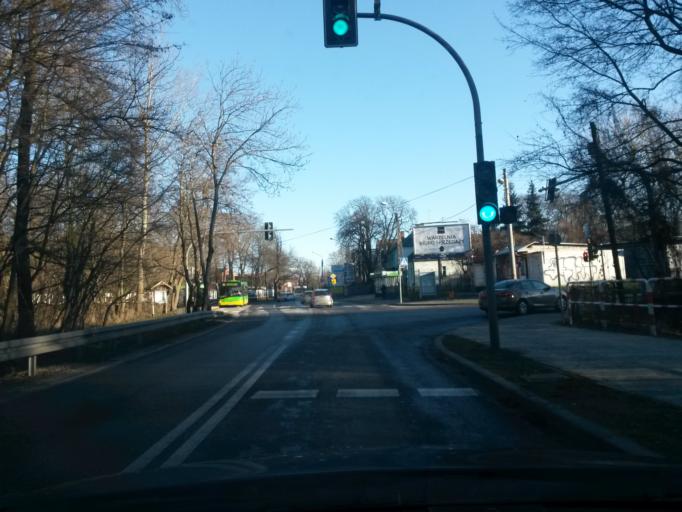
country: PL
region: Greater Poland Voivodeship
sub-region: Powiat poznanski
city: Swarzedz
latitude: 52.3926
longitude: 17.0140
